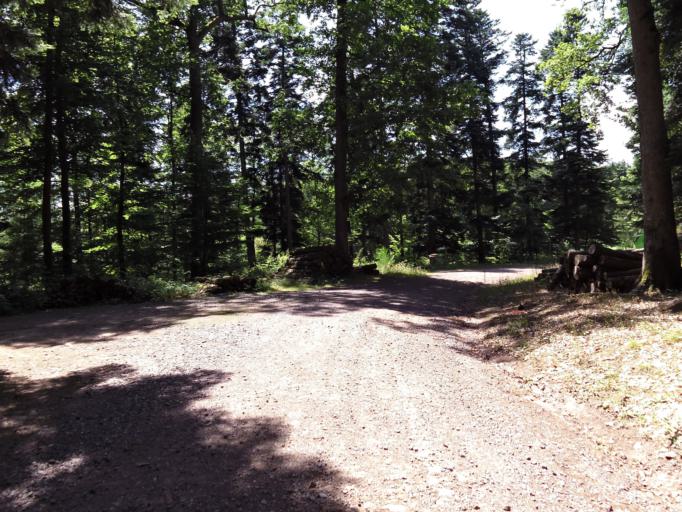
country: DE
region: Rheinland-Pfalz
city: Wilgartswiesen
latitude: 49.2629
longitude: 7.8723
